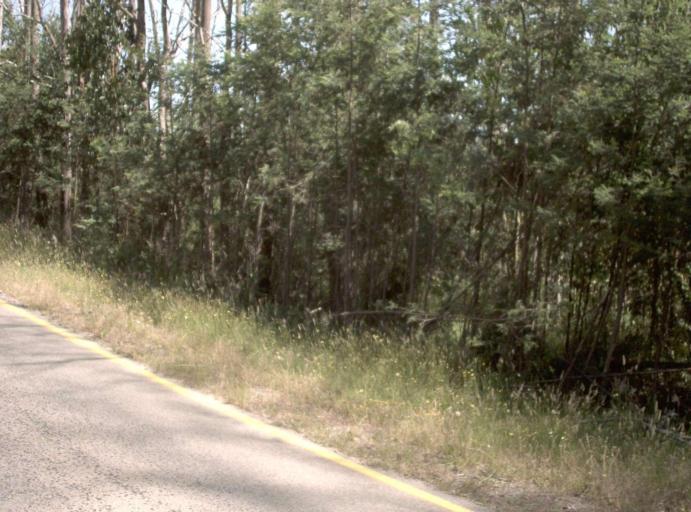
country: AU
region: Victoria
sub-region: Yarra Ranges
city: Millgrove
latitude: -37.5599
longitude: 145.8848
